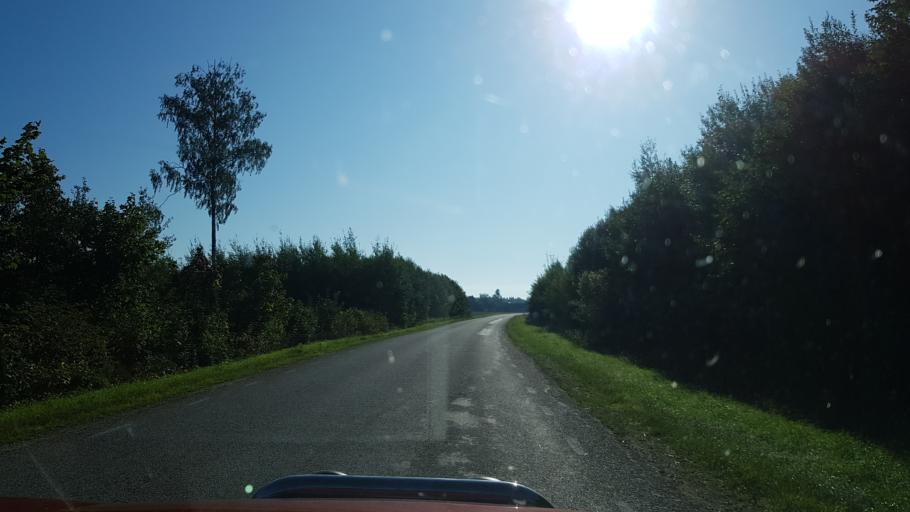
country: EE
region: Jogevamaa
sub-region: Tabivere vald
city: Tabivere
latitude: 58.6844
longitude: 26.6038
